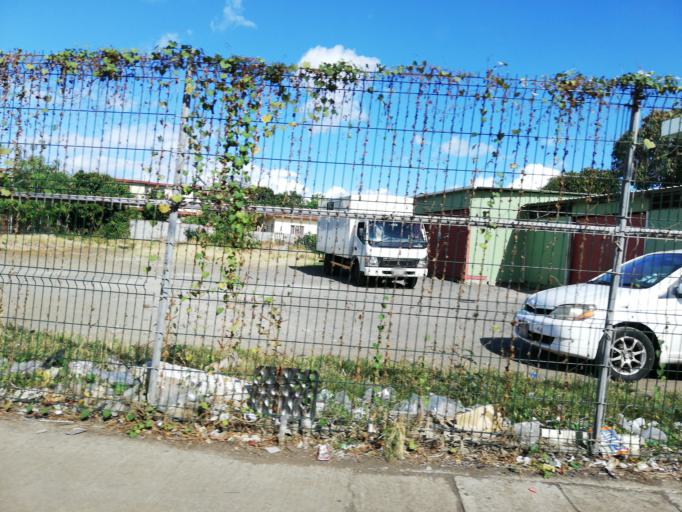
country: MU
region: Moka
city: Pailles
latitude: -20.1766
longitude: 57.4741
